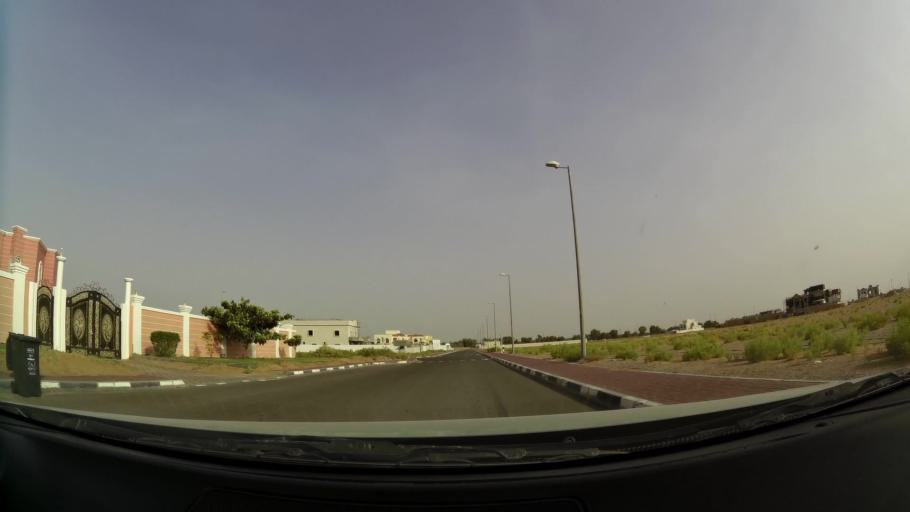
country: AE
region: Abu Dhabi
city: Al Ain
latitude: 24.2096
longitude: 55.6372
